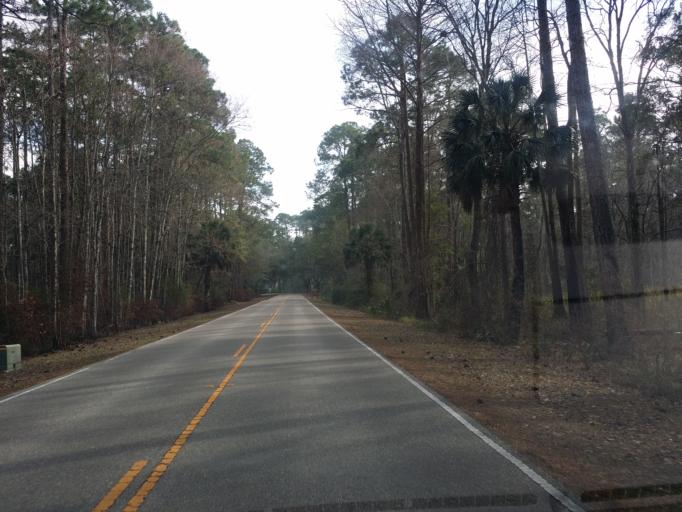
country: US
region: Florida
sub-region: Leon County
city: Woodville
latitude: 30.1534
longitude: -84.1490
